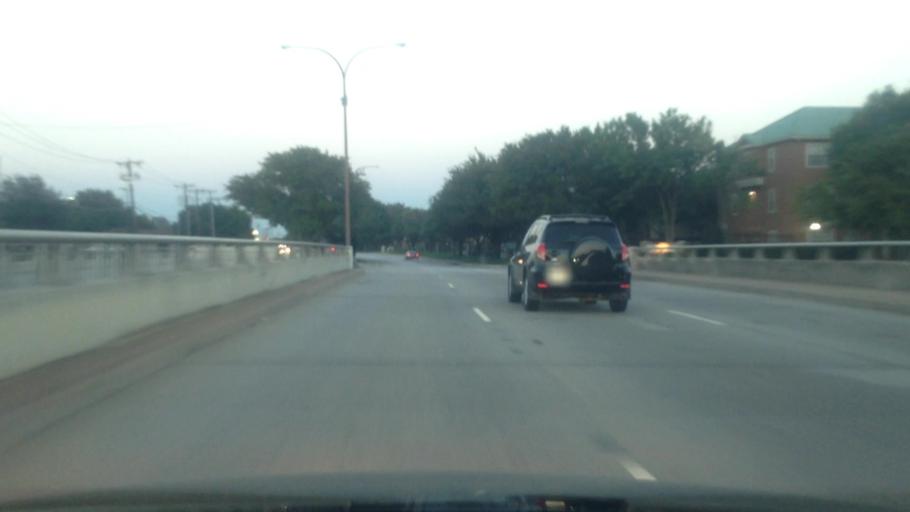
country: US
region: Texas
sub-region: Tarrant County
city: Blue Mound
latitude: 32.8608
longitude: -97.3123
